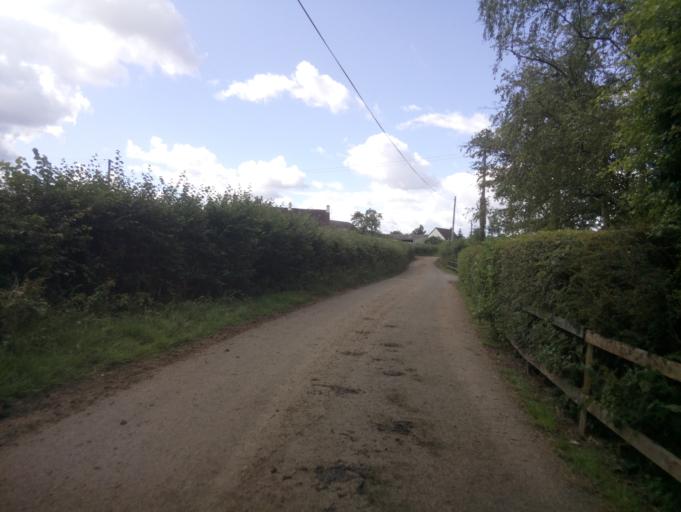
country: GB
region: England
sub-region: Gloucestershire
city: Newent
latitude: 51.8471
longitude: -2.3603
